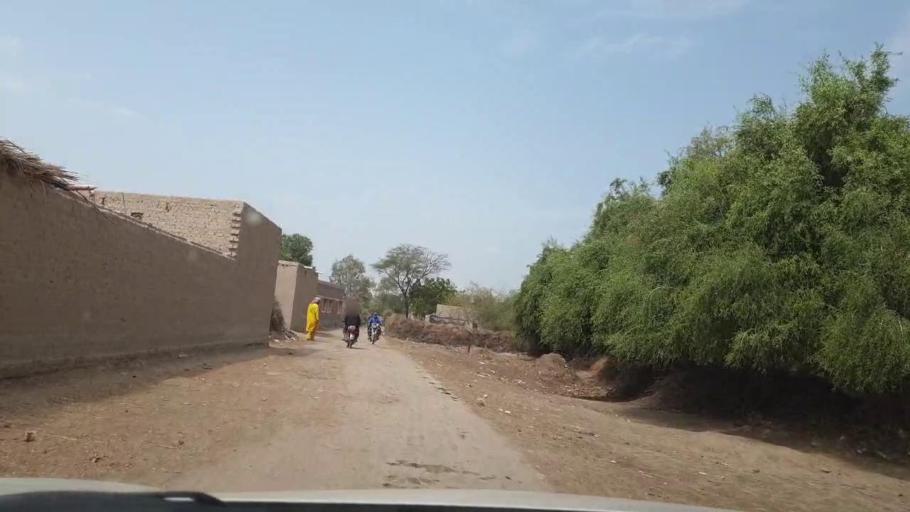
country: PK
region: Sindh
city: Sobhadero
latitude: 27.3872
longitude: 68.2767
